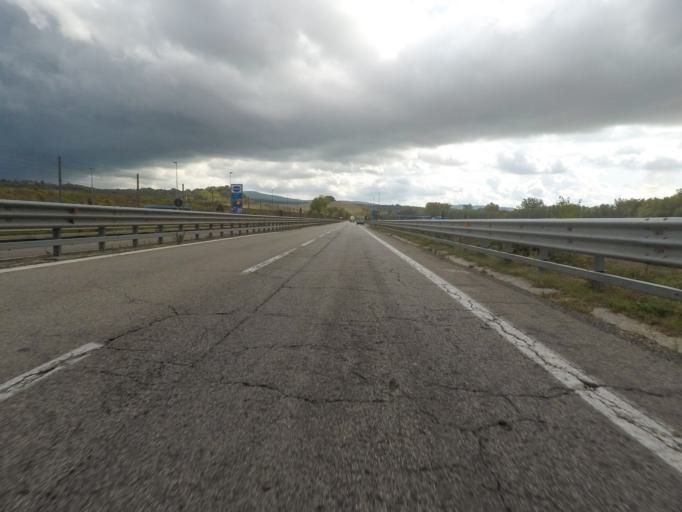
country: IT
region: Tuscany
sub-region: Provincia di Siena
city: Rapolano Terme
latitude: 43.3237
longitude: 11.5632
